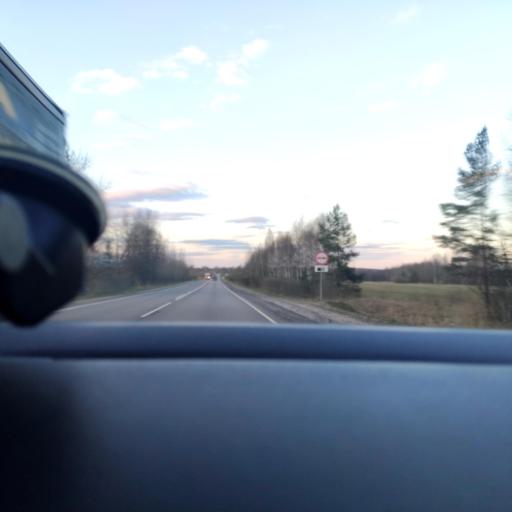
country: RU
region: Moskovskaya
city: Krasnyy Tkach
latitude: 55.4192
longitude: 39.1816
